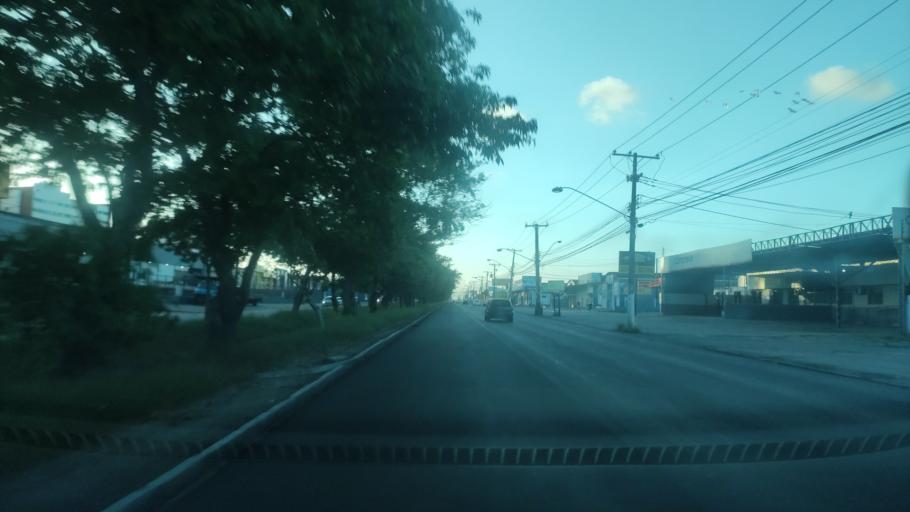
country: BR
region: Alagoas
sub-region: Satuba
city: Satuba
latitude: -9.5804
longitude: -35.7675
